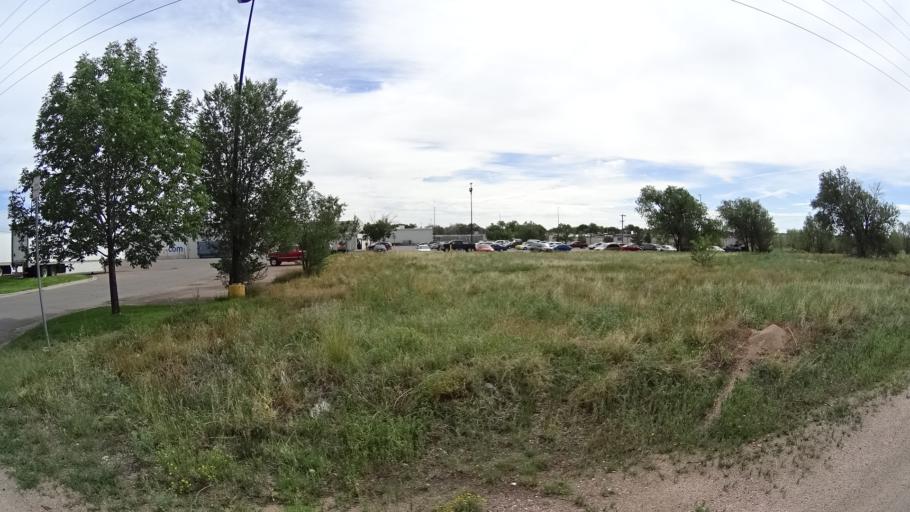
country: US
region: Colorado
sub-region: El Paso County
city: Security-Widefield
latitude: 38.7390
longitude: -104.7375
